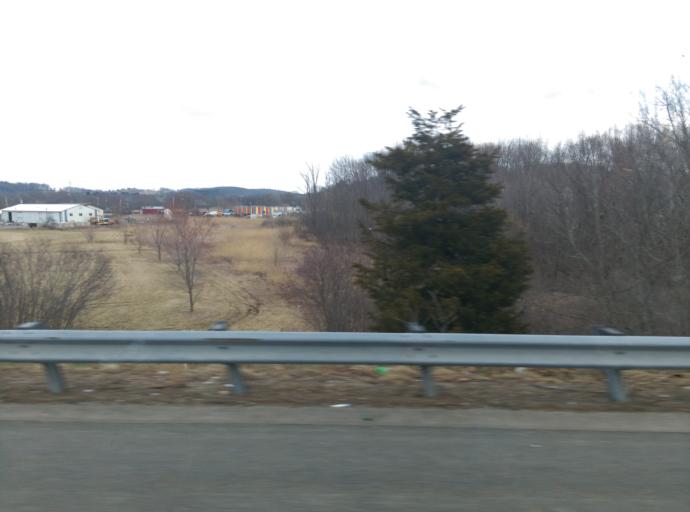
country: US
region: Massachusetts
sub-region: Essex County
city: North Andover
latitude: 42.7511
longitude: -71.1312
